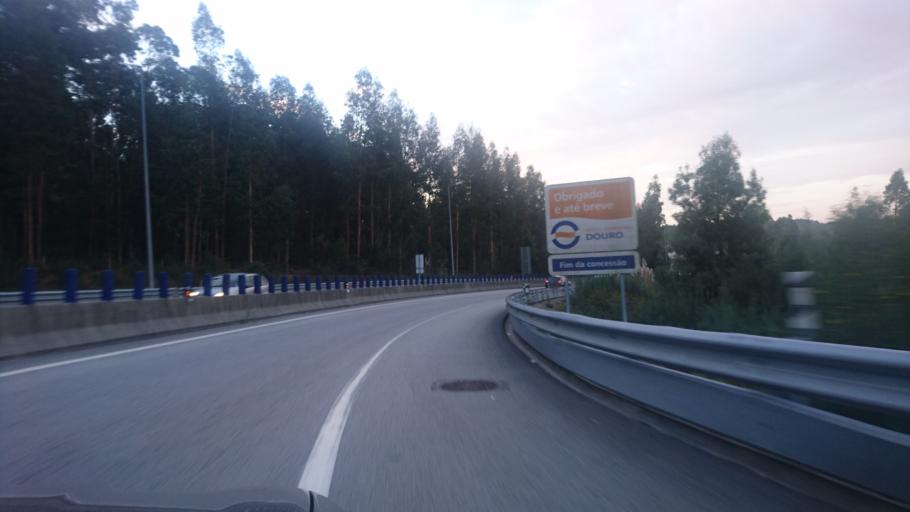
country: PT
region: Aveiro
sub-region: Santa Maria da Feira
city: Milheiros de Poiares
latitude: 40.9400
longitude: -8.4735
